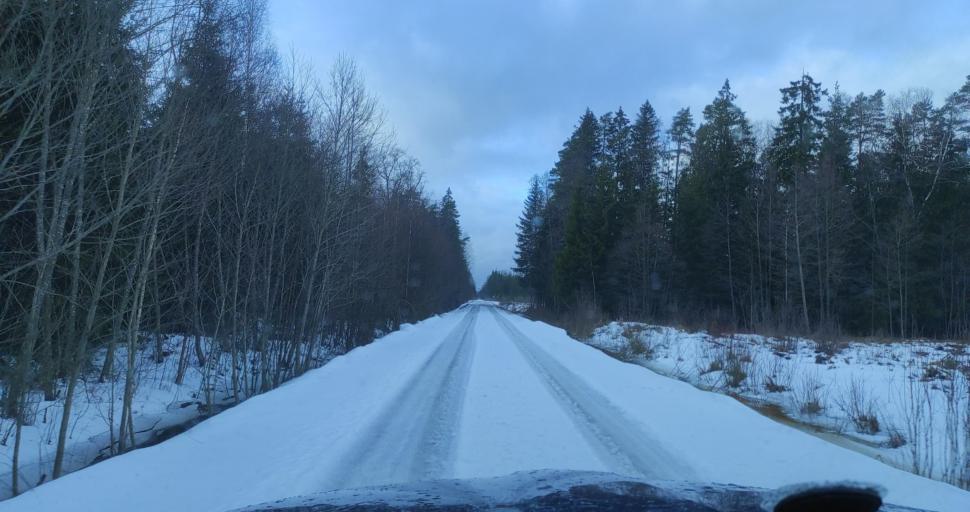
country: LV
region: Dundaga
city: Dundaga
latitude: 57.4104
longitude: 22.0830
